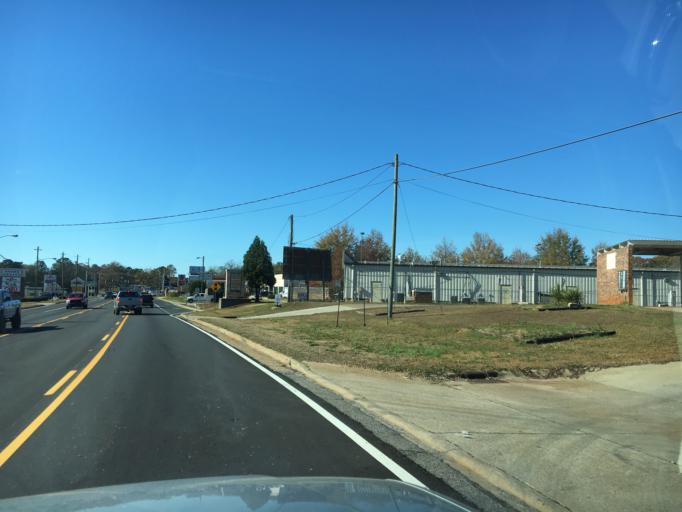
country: US
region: Georgia
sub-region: Hart County
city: Hartwell
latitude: 34.3547
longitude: -82.9091
